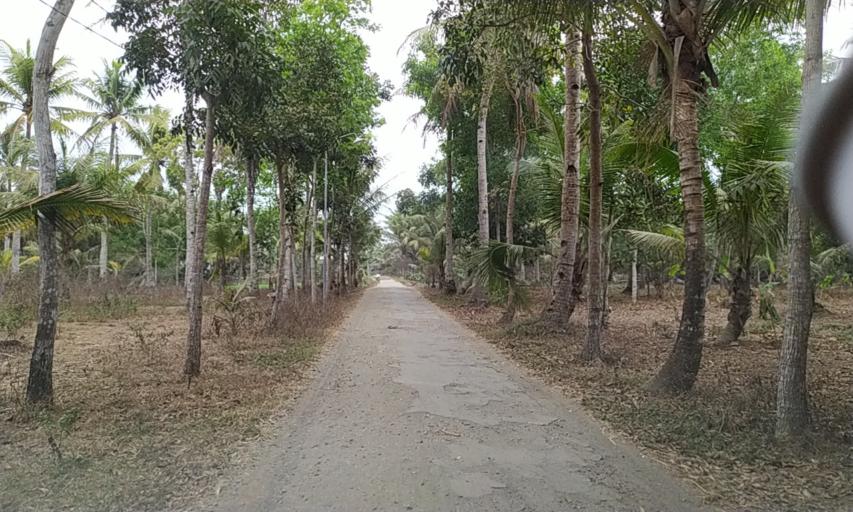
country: ID
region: Central Java
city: Kroya
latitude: -7.7000
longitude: 109.3123
